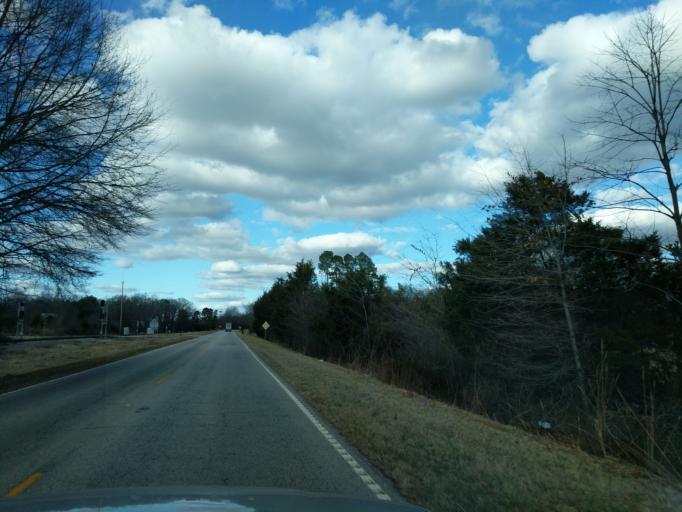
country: US
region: South Carolina
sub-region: Laurens County
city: Watts Mills
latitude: 34.5904
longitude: -81.9947
